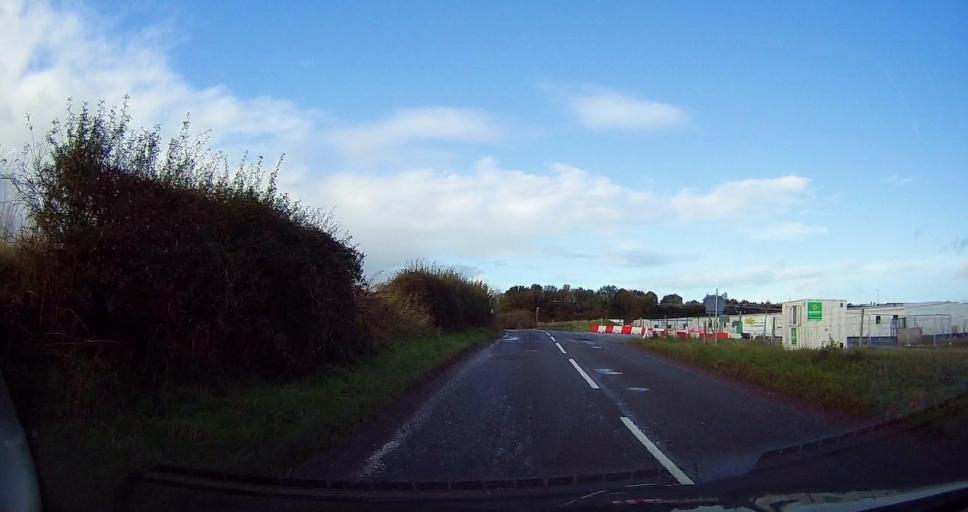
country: GB
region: England
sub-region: Staffordshire
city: Whittington
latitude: 52.6821
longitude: -1.7910
